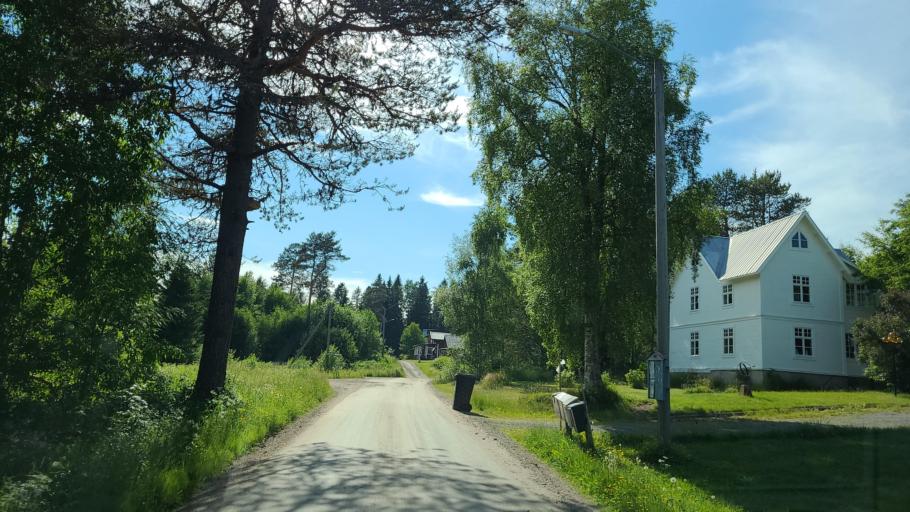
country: SE
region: Vaesterbotten
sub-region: Robertsfors Kommun
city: Robertsfors
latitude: 64.1623
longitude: 20.9673
